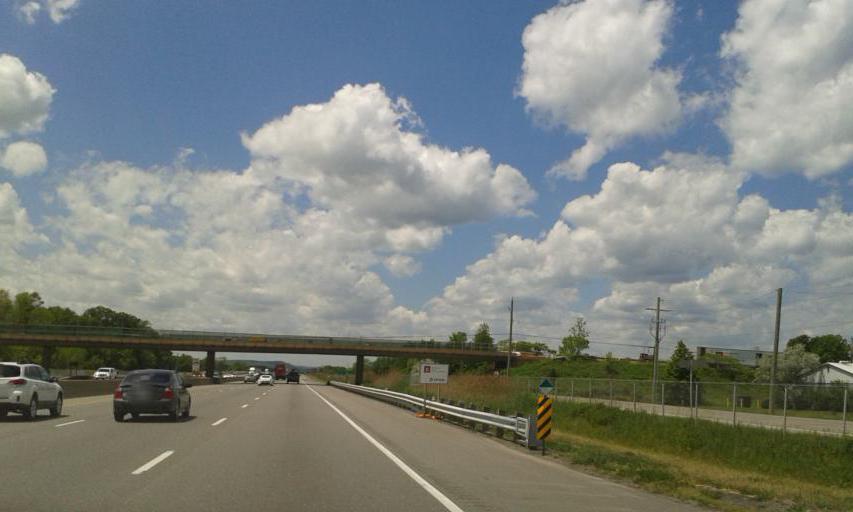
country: CA
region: Ontario
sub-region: Regional Municipality of Niagara
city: St. Catharines
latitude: 43.1881
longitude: -79.4439
